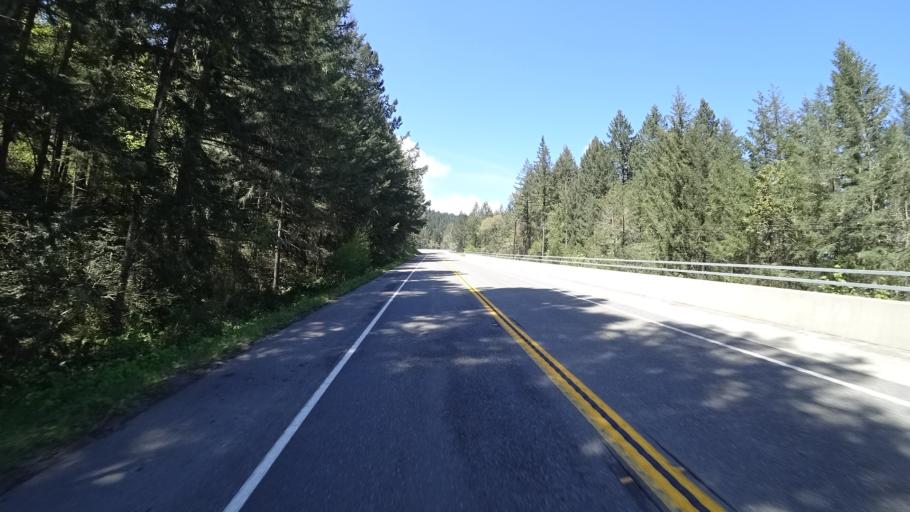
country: US
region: California
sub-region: Humboldt County
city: Blue Lake
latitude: 40.9159
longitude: -123.8268
